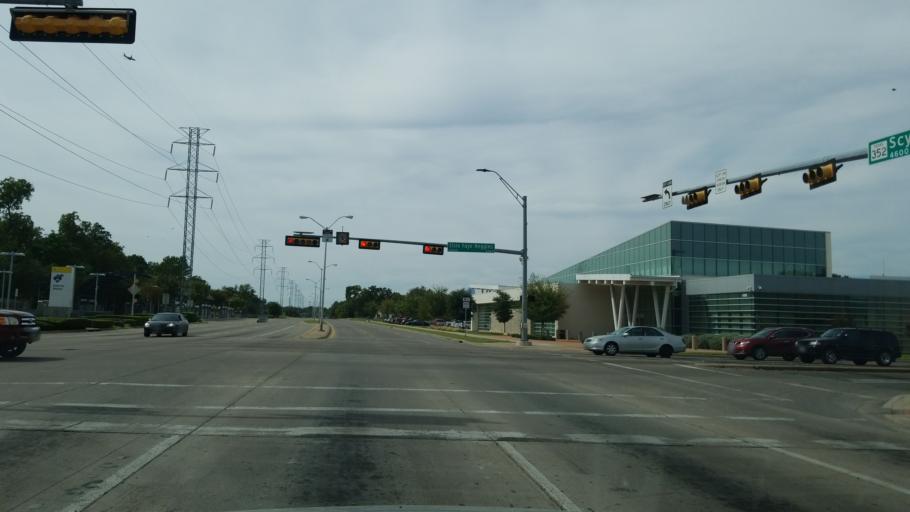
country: US
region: Texas
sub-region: Dallas County
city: Dallas
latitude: 32.7662
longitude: -96.7404
